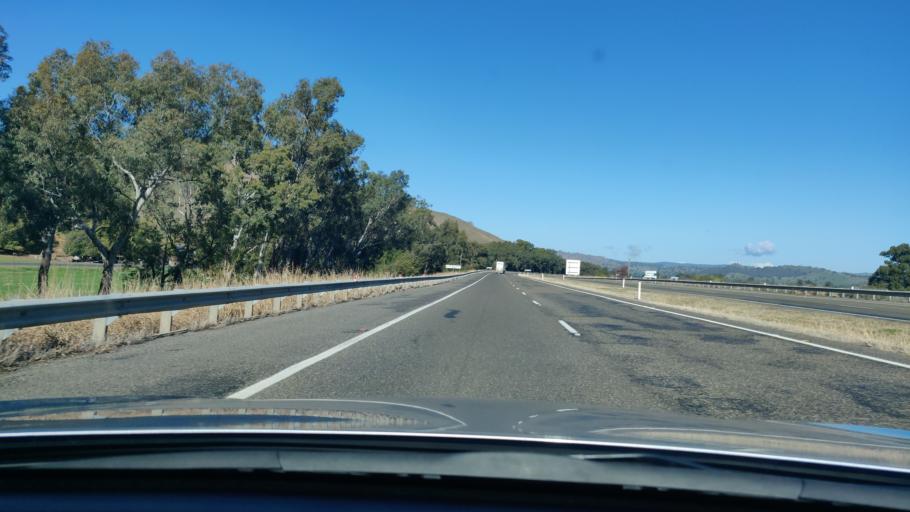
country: AU
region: New South Wales
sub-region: Gundagai
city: Gundagai
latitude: -35.0945
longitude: 148.0745
